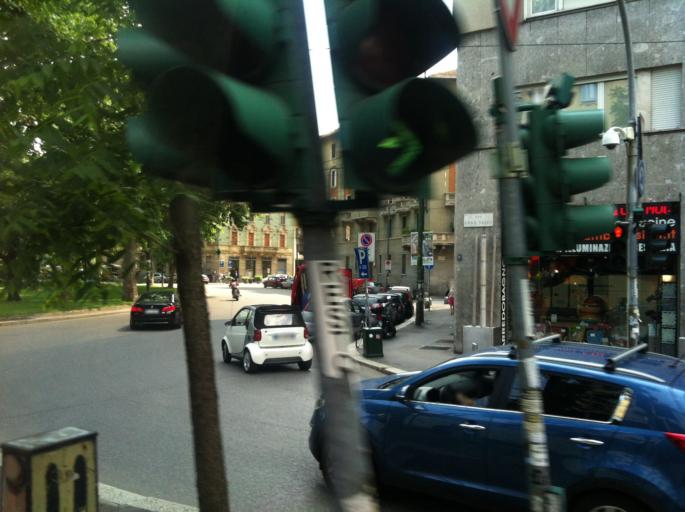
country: IT
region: Lombardy
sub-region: Citta metropolitana di Milano
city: Milano
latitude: 45.4806
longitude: 9.2227
